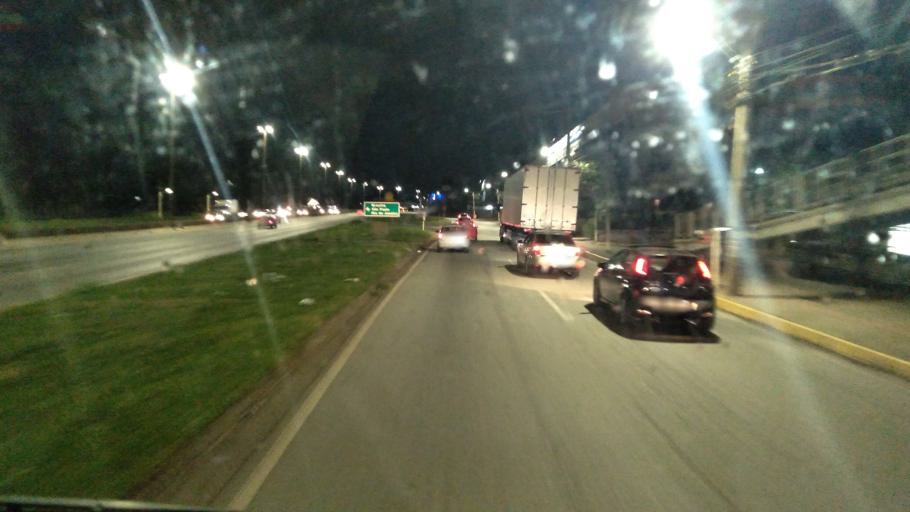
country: BR
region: Minas Gerais
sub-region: Belo Horizonte
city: Belo Horizonte
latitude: -19.8988
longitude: -43.9818
